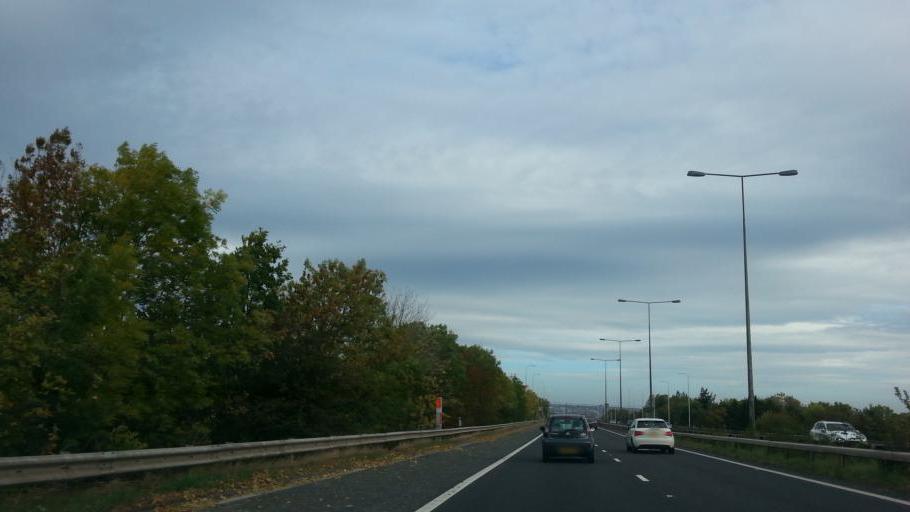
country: GB
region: England
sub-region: City and Borough of Leeds
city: Morley
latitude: 53.7664
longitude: -1.5942
